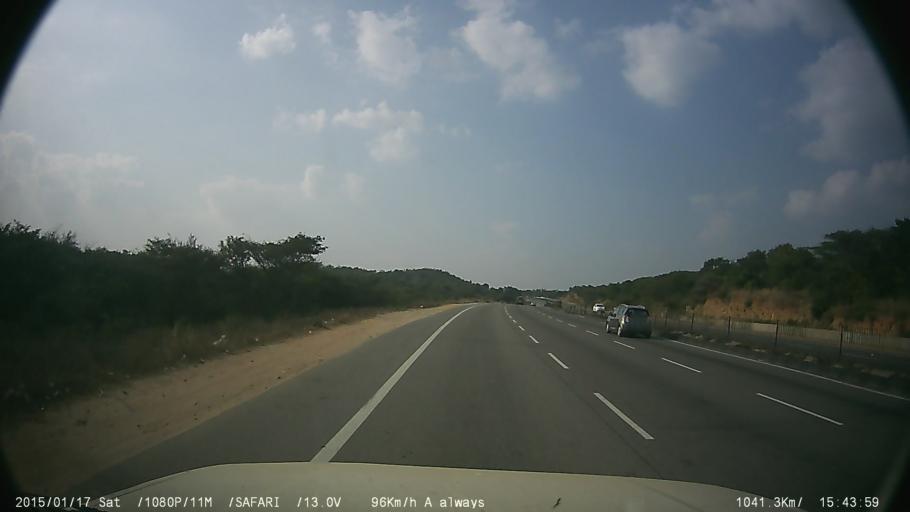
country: IN
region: Tamil Nadu
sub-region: Krishnagiri
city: Hosur
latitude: 12.6928
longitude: 77.9181
